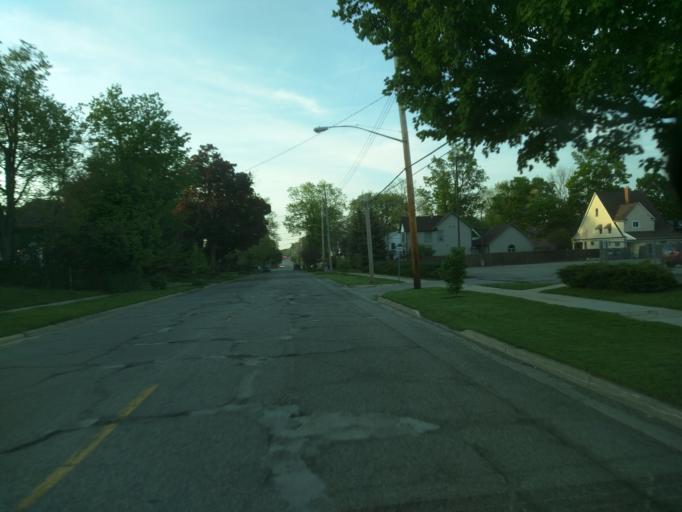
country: US
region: Michigan
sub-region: Ingham County
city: Lansing
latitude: 42.7451
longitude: -84.5553
